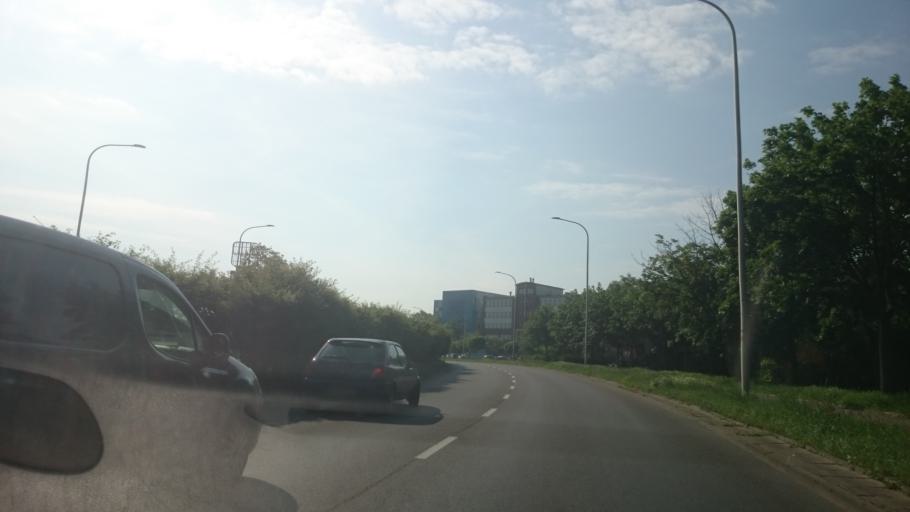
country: PL
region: Opole Voivodeship
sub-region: Powiat opolski
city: Opole
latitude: 50.6716
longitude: 17.9387
